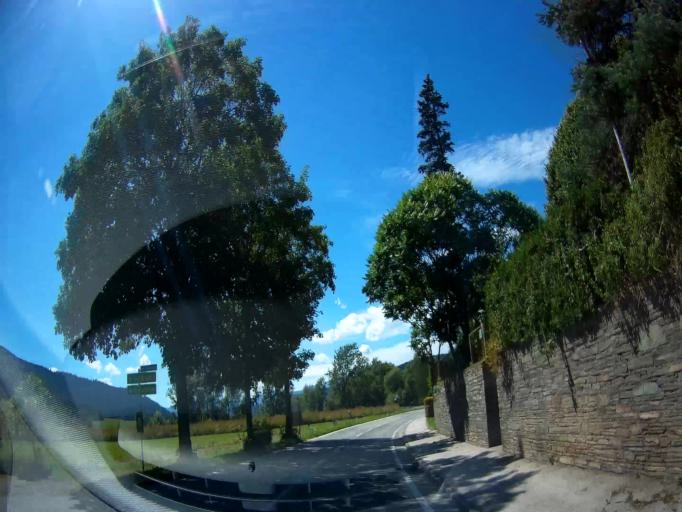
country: AT
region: Carinthia
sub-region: Politischer Bezirk Sankt Veit an der Glan
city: Glodnitz
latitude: 46.8499
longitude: 14.1896
